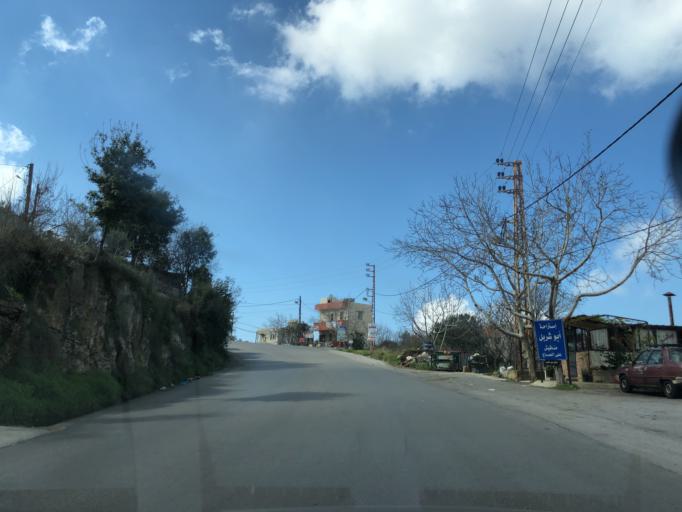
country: LB
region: Mont-Liban
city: Jbail
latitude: 34.1204
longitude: 35.7038
